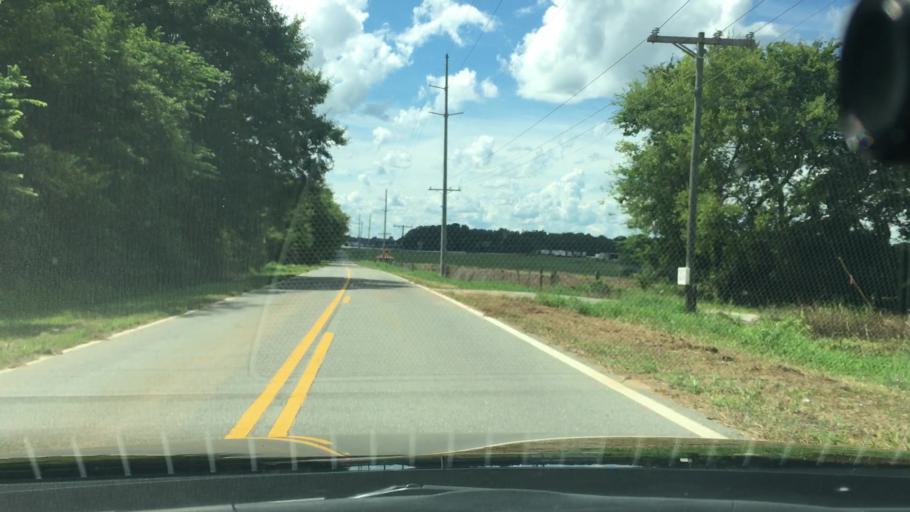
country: US
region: Georgia
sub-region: Putnam County
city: Jefferson
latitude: 33.3733
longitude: -83.2976
